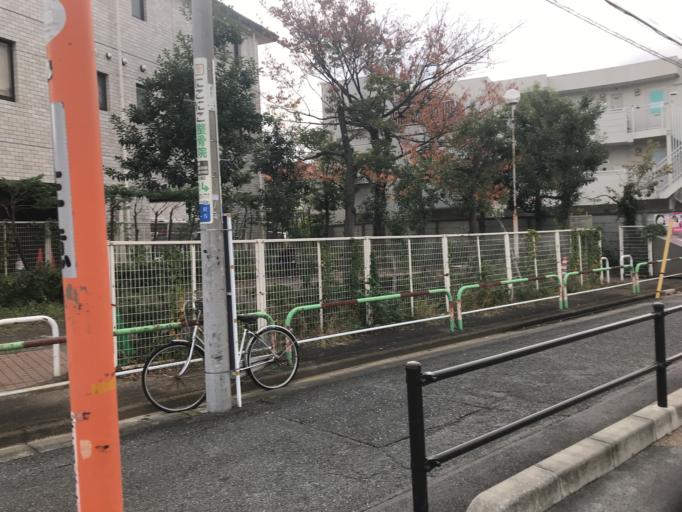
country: JP
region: Tokyo
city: Tokyo
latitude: 35.6073
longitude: 139.6654
